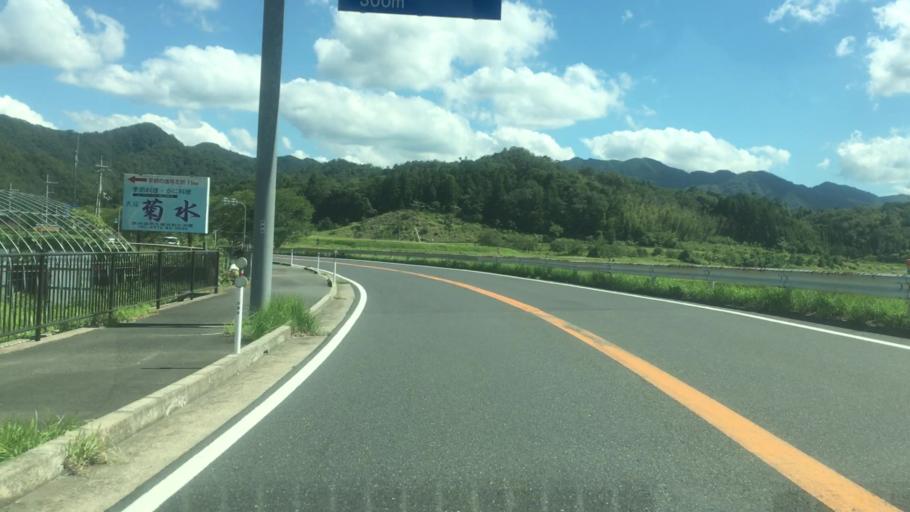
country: JP
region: Hyogo
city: Toyooka
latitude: 35.5752
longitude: 134.9754
